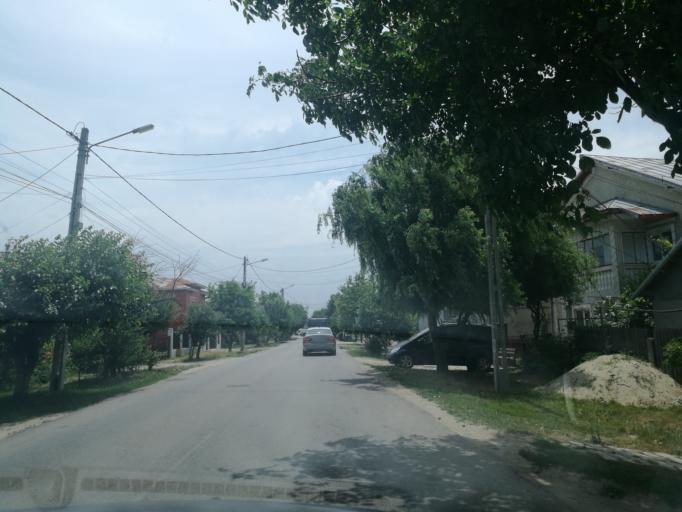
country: RO
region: Ilfov
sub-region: Comuna Vidra
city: Cretesti
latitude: 44.2813
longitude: 26.1338
